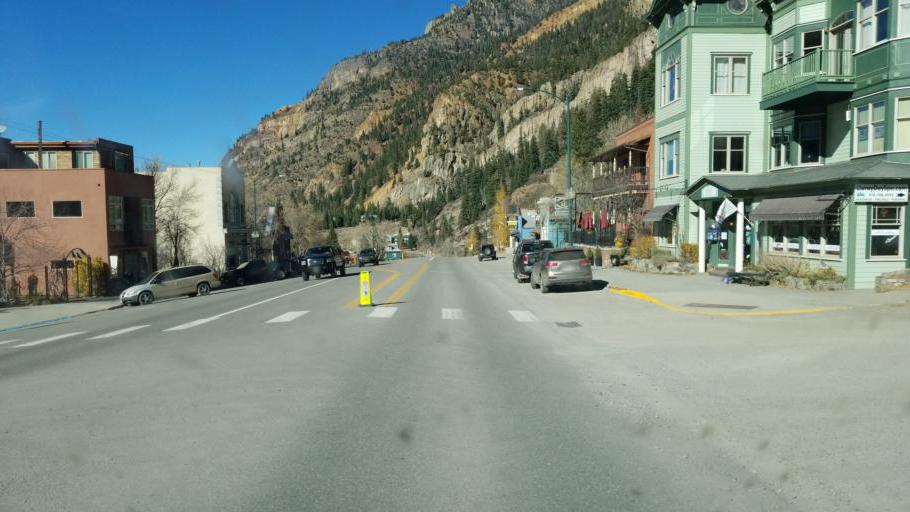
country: US
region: Colorado
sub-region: Ouray County
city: Ouray
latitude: 38.0250
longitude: -107.6714
